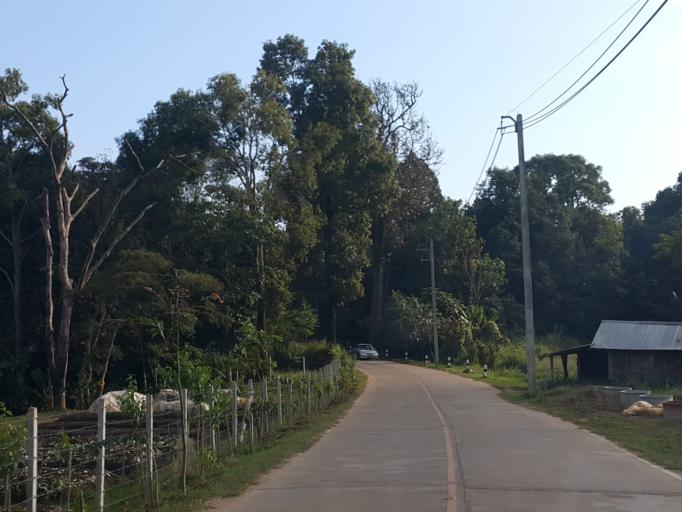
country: TH
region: Chiang Mai
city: Samoeng
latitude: 18.9293
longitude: 98.8200
